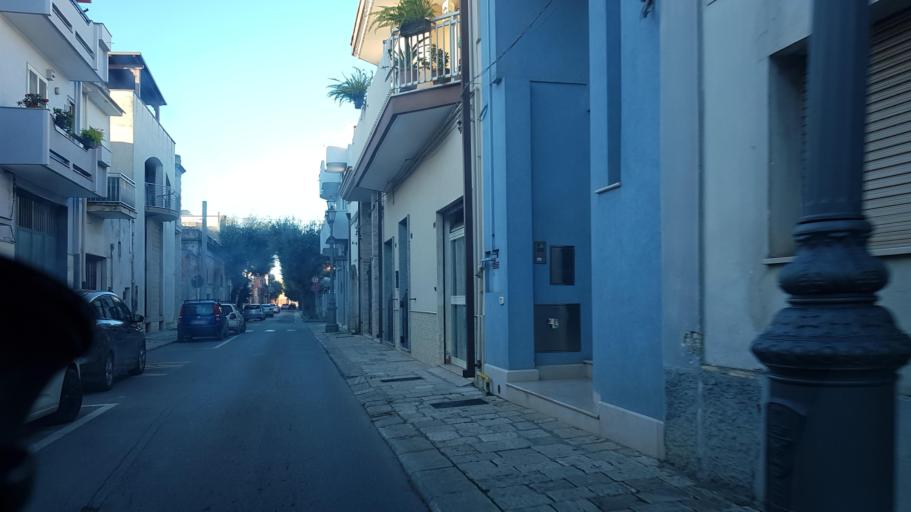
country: IT
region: Apulia
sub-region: Provincia di Brindisi
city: Latiano
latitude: 40.5557
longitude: 17.7186
